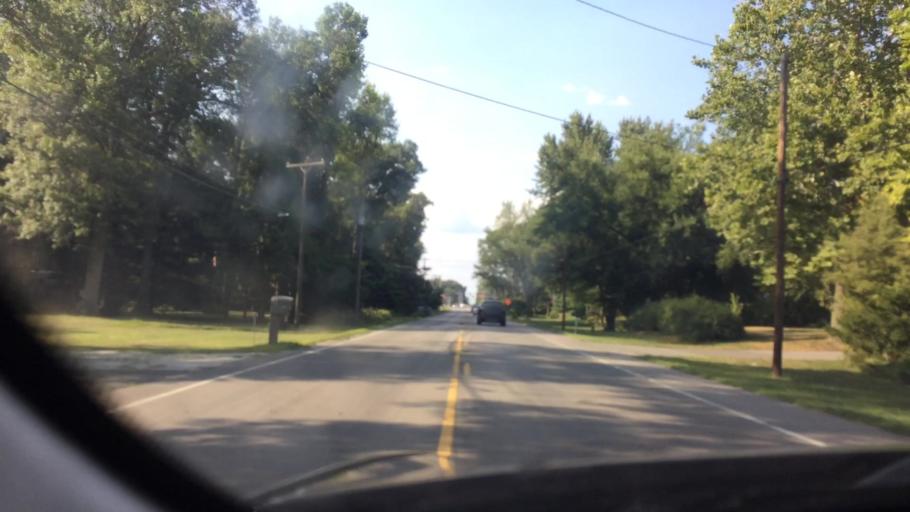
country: US
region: Ohio
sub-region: Lucas County
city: Holland
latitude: 41.6702
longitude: -83.7226
